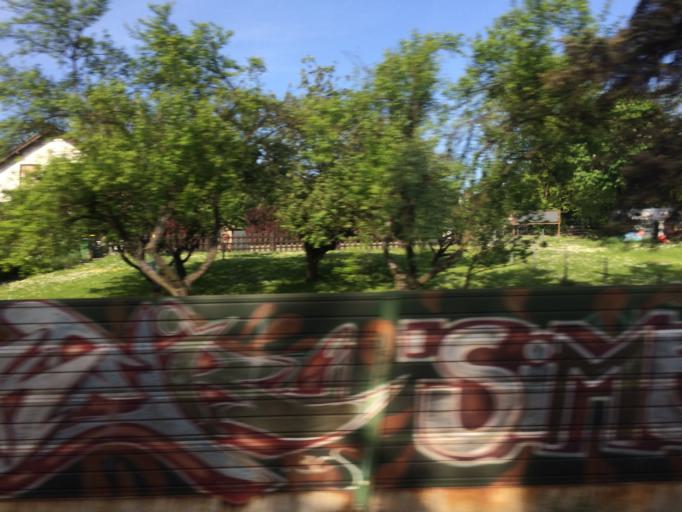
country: DE
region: North Rhine-Westphalia
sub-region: Regierungsbezirk Koln
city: Konigswinter
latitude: 50.7055
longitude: 7.1707
